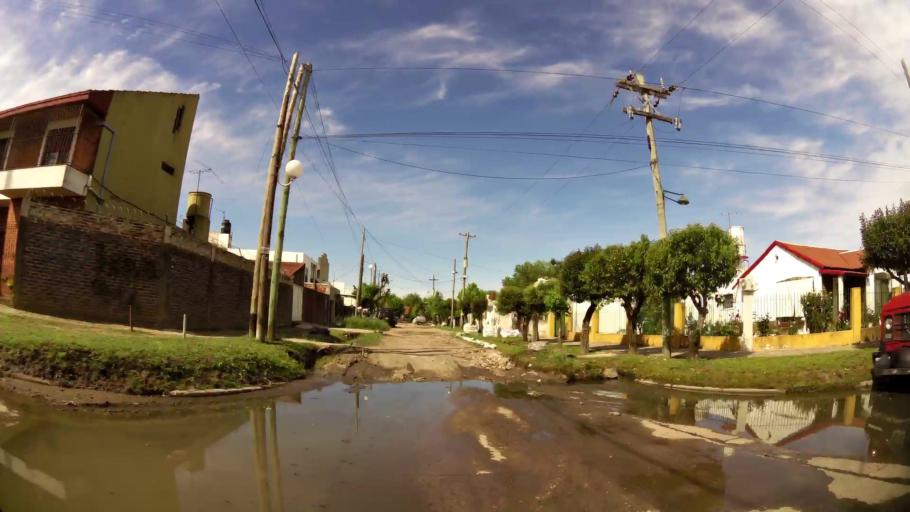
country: AR
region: Buenos Aires
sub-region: Partido de Quilmes
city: Quilmes
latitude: -34.7763
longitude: -58.3028
